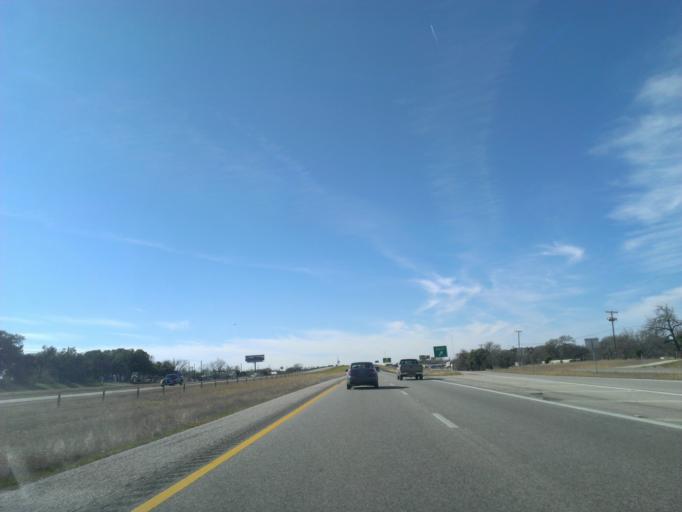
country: US
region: Texas
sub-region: Bell County
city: Belton
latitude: 31.0559
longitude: -97.5262
